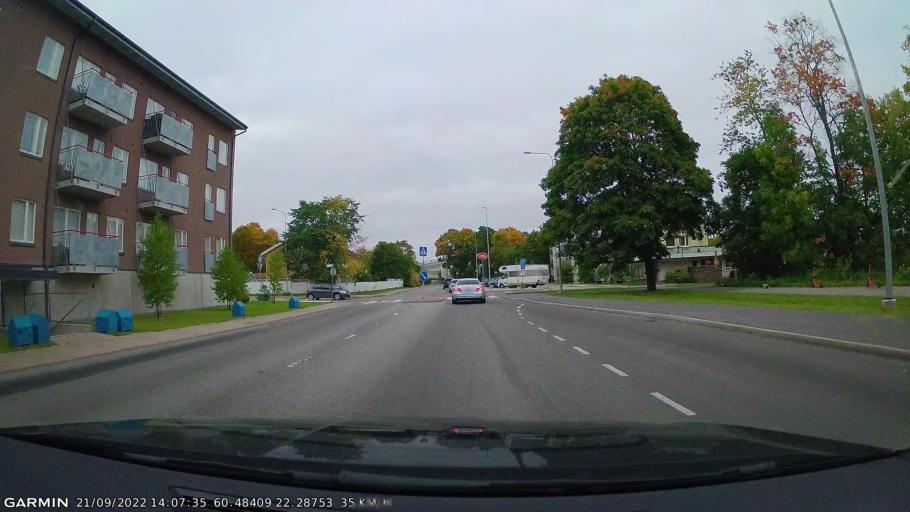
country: FI
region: Varsinais-Suomi
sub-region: Turku
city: Turku
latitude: 60.4842
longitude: 22.2875
